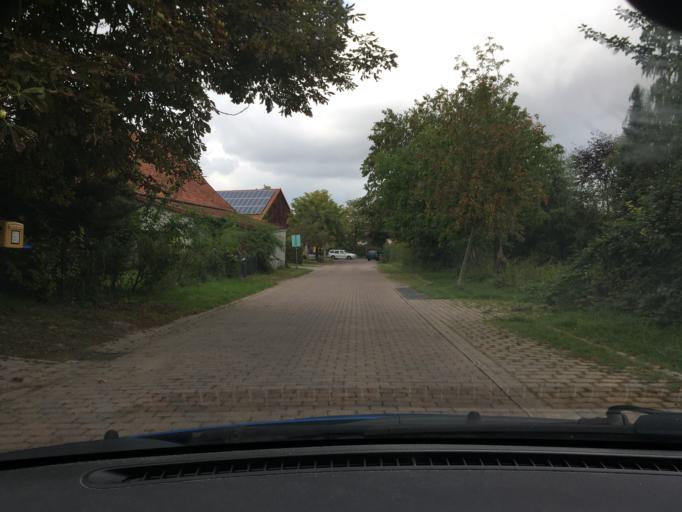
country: DE
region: Lower Saxony
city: Messenkamp
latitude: 52.2188
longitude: 9.4050
